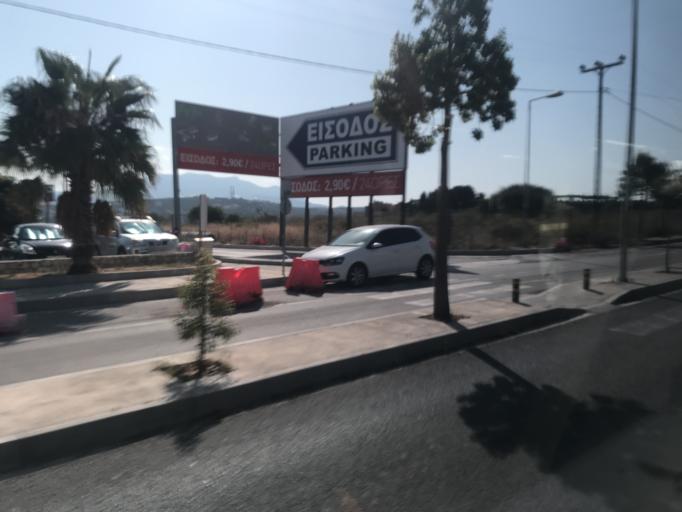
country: GR
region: Crete
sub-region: Nomos Irakleiou
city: Gazi
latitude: 35.3037
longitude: 25.0850
